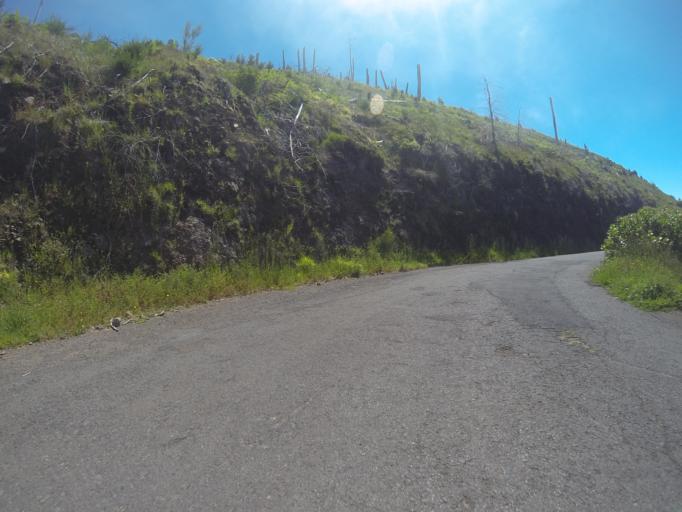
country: PT
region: Madeira
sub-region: Funchal
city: Nossa Senhora do Monte
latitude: 32.7029
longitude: -16.9090
